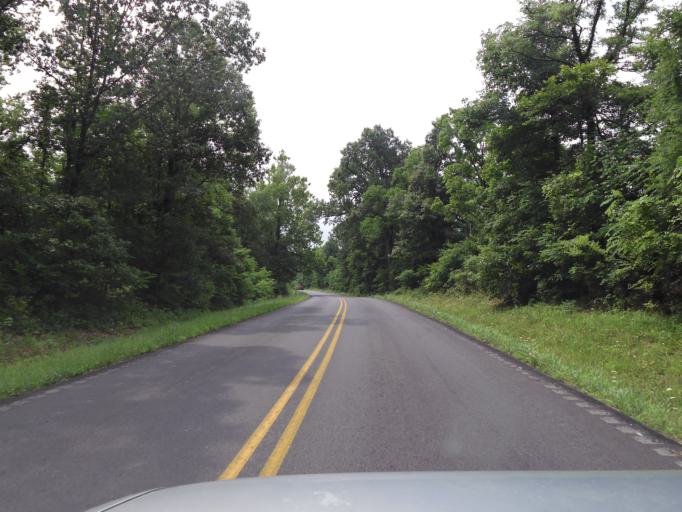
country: US
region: Kentucky
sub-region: Hopkins County
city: Madisonville
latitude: 37.3031
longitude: -87.3671
